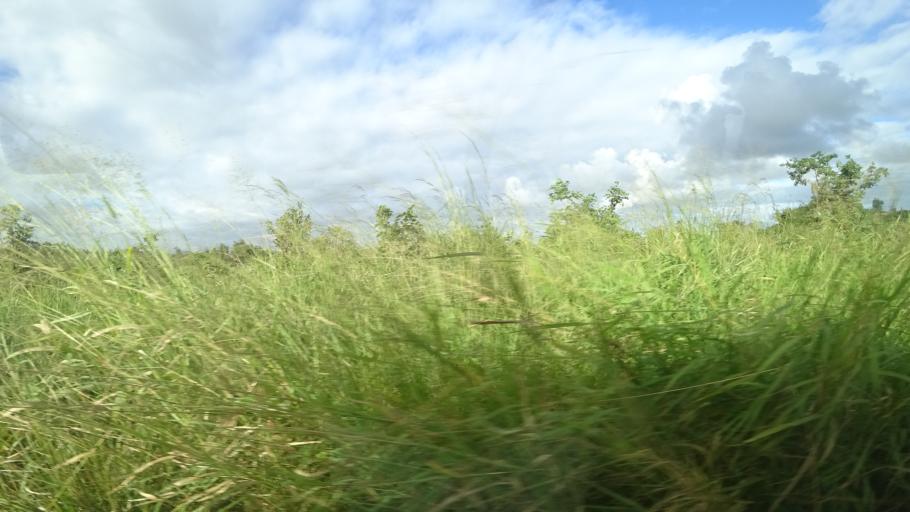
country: MZ
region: Sofala
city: Beira
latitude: -19.6507
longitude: 35.0583
